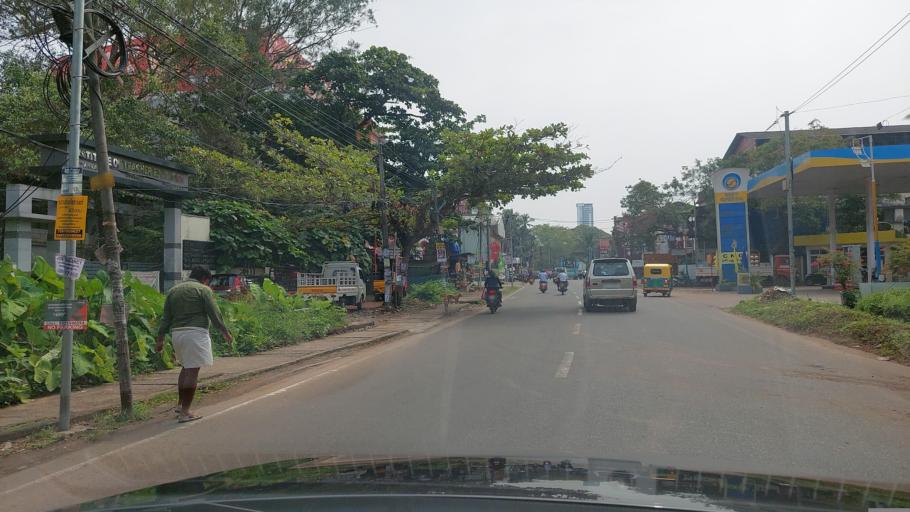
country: IN
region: Kerala
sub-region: Kozhikode
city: Kozhikode
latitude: 11.2712
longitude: 75.7778
